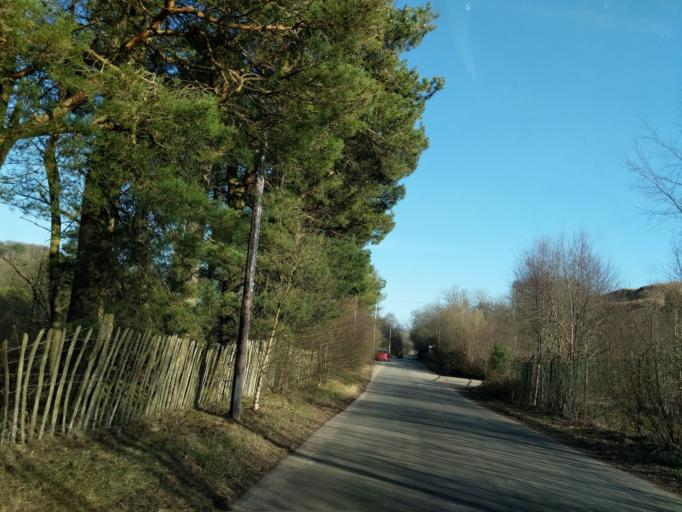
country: GB
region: Scotland
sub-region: The Scottish Borders
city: West Linton
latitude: 55.7204
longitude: -3.4326
